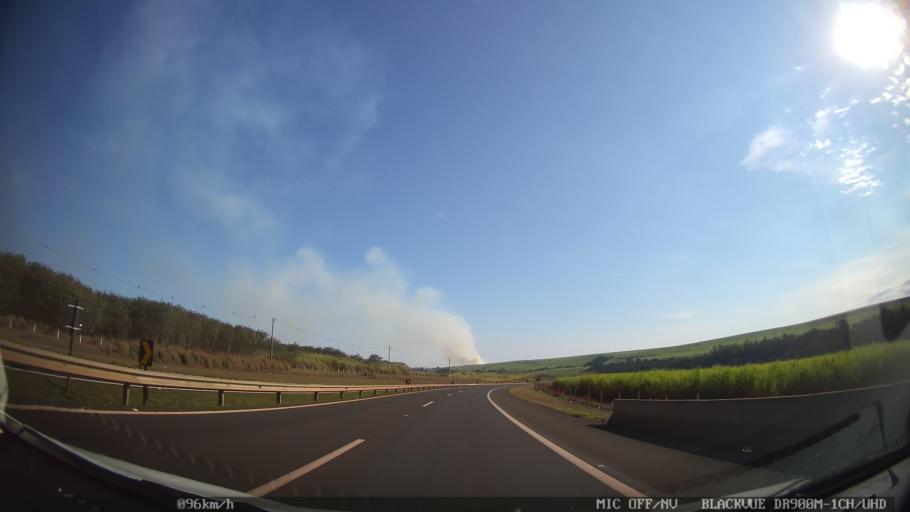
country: BR
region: Sao Paulo
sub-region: Piracicaba
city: Piracicaba
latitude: -22.6821
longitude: -47.5710
